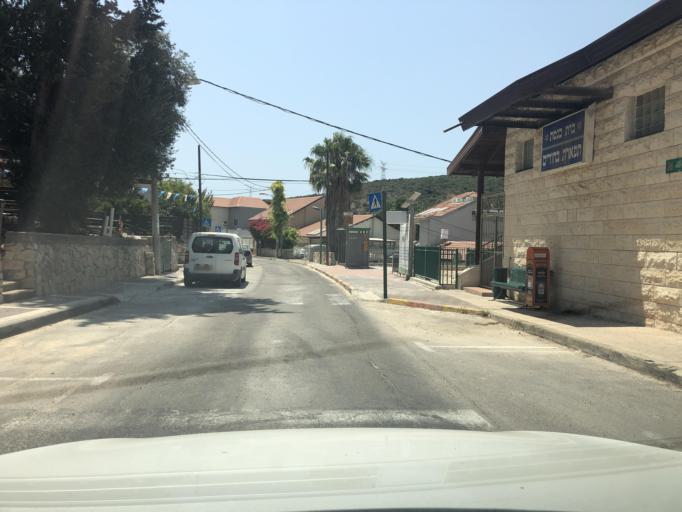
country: IL
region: Haifa
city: Daliyat el Karmil
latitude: 32.6619
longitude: 35.1092
